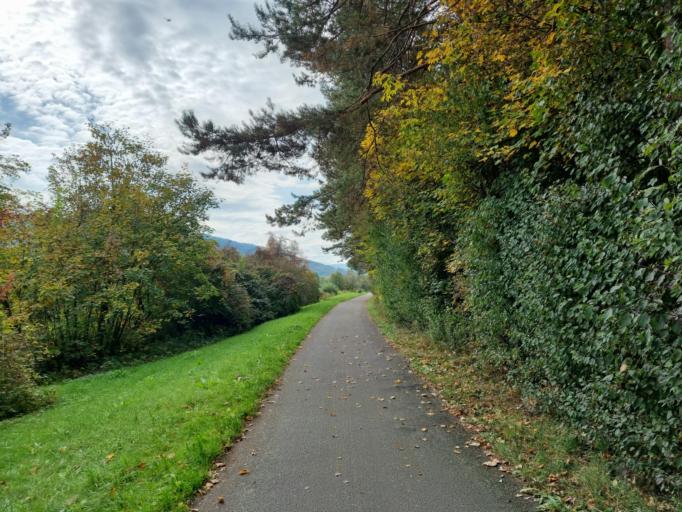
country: AT
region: Lower Austria
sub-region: Politischer Bezirk Sankt Polten
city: Wilhelmsburg
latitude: 48.1246
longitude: 15.6278
